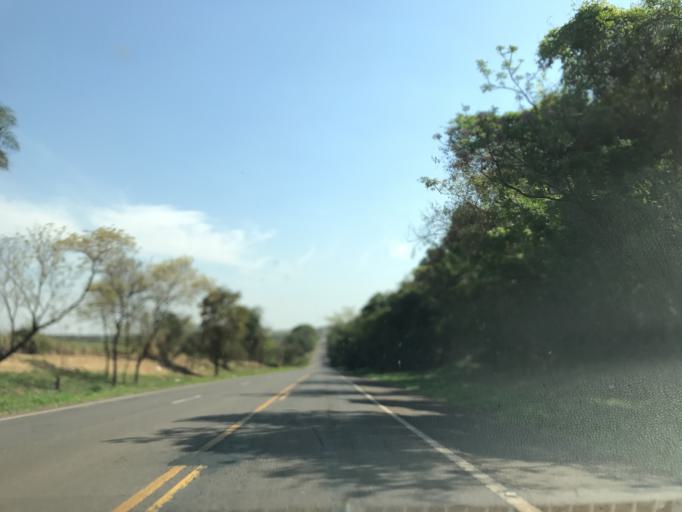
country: BR
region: Sao Paulo
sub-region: Jose Bonifacio
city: Jose Bonifacio
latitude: -21.0698
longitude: -49.7482
